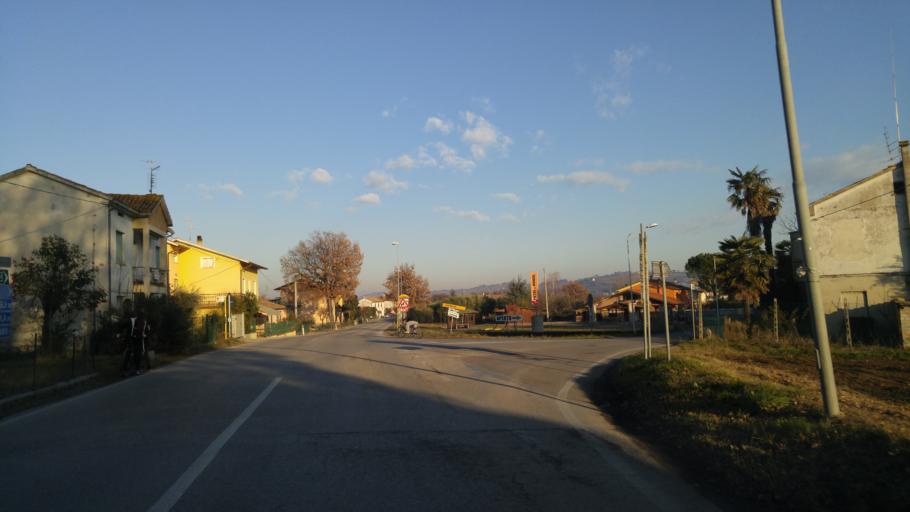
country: IT
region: The Marches
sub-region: Provincia di Pesaro e Urbino
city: San Michele
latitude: 43.6666
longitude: 13.0079
